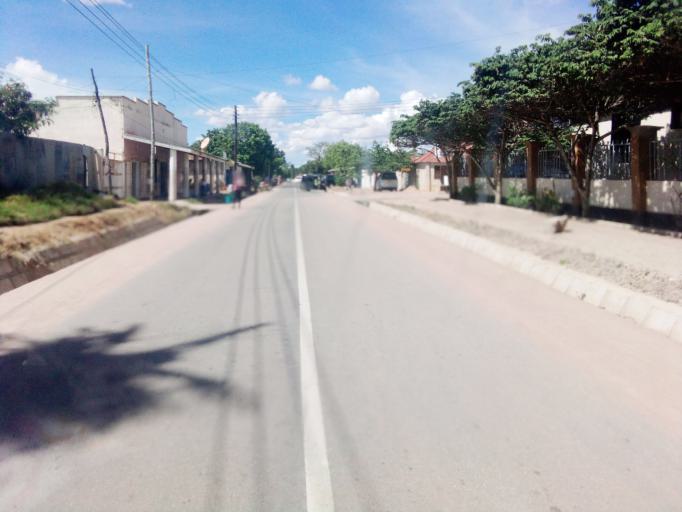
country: TZ
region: Dodoma
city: Dodoma
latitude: -6.1740
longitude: 35.7578
